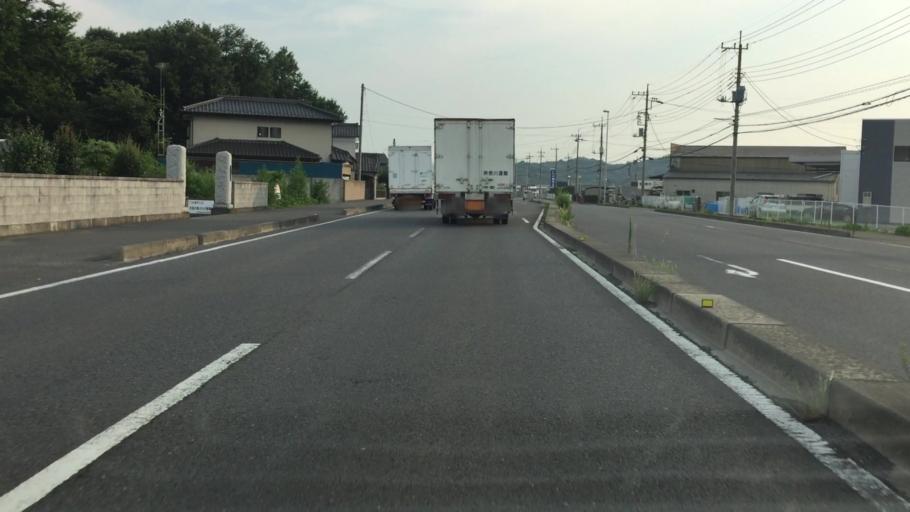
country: JP
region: Tochigi
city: Tochigi
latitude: 36.3242
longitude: 139.6802
